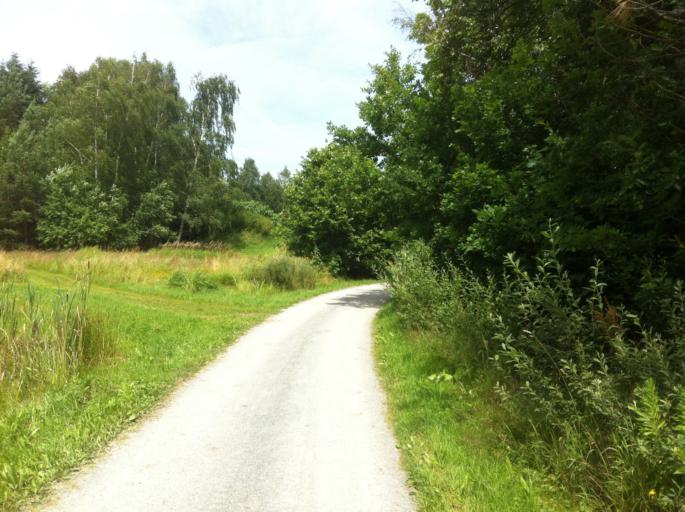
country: DE
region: Bavaria
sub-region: Upper Franconia
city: Bayreuth
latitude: 49.9230
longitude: 11.5833
